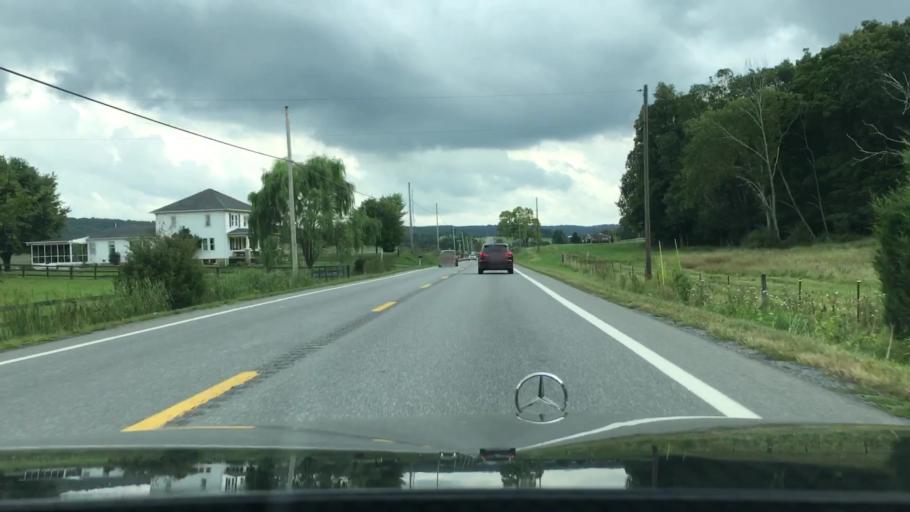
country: US
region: West Virginia
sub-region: Morgan County
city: Berkeley Springs
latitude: 39.4558
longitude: -78.3107
